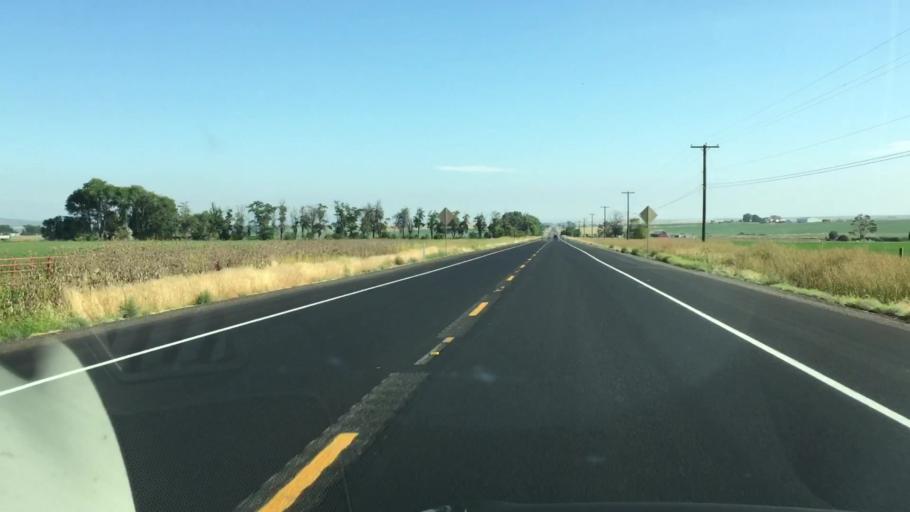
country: US
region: Oregon
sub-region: Jefferson County
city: Culver
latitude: 44.5032
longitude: -121.1893
